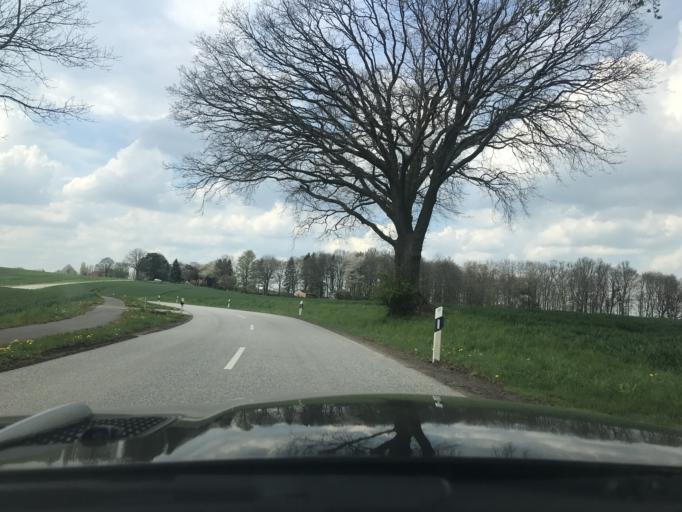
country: DE
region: Schleswig-Holstein
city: Schashagen
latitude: 54.1015
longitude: 10.8788
